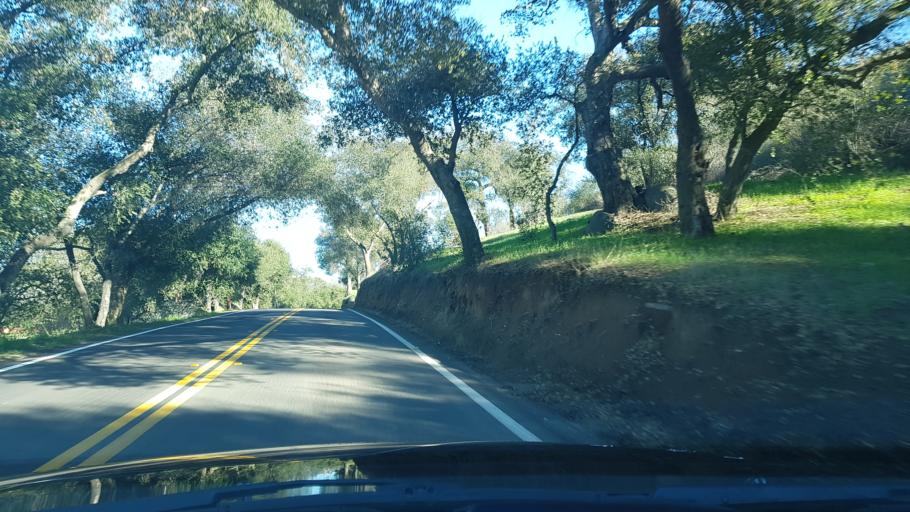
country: US
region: California
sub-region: San Diego County
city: Valley Center
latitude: 33.2054
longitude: -116.9791
